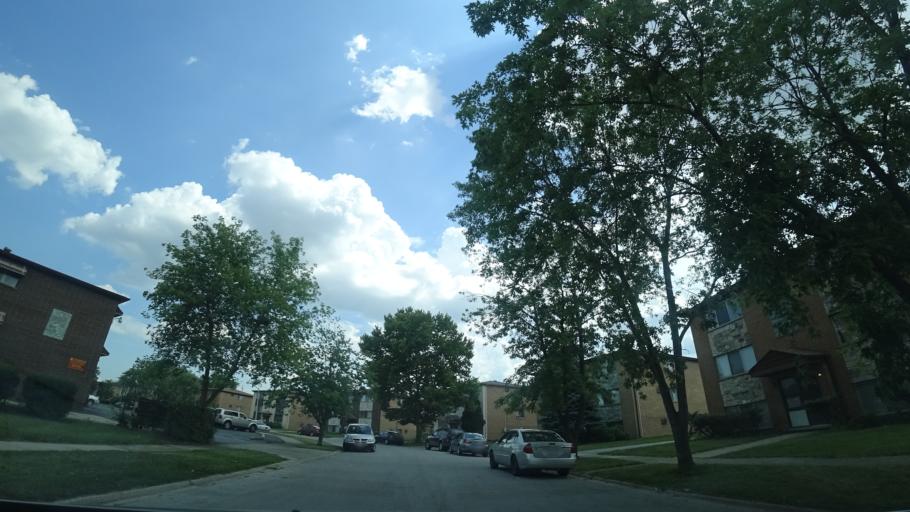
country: US
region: Illinois
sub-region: Cook County
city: Alsip
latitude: 41.6679
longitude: -87.7185
